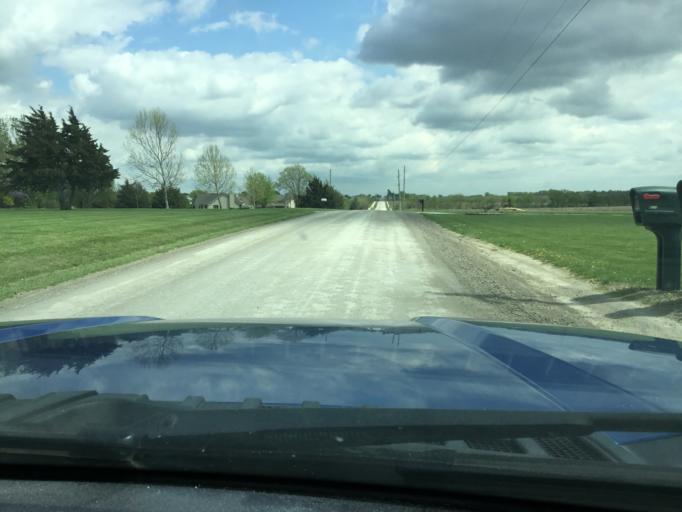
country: US
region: Kansas
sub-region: Douglas County
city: Eudora
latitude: 38.9132
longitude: -95.1075
